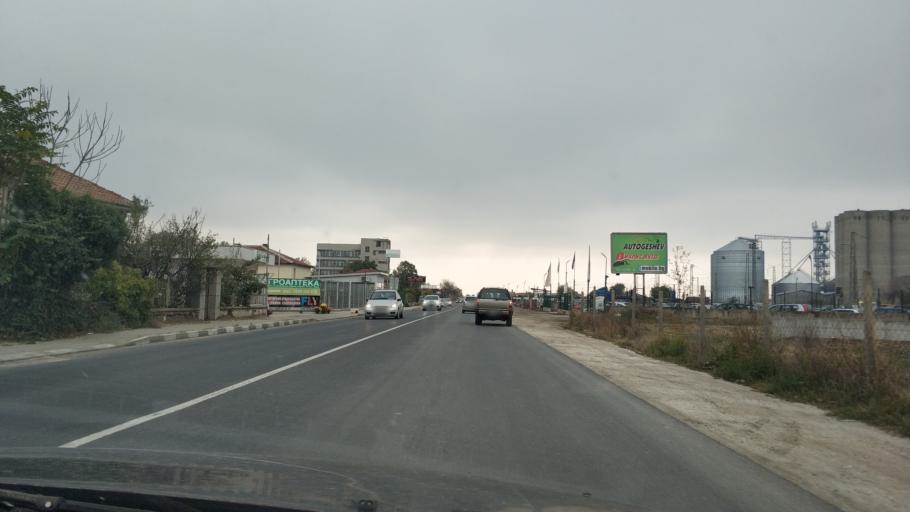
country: BG
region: Plovdiv
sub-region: Obshtina Plovdiv
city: Plovdiv
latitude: 42.2288
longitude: 24.7248
